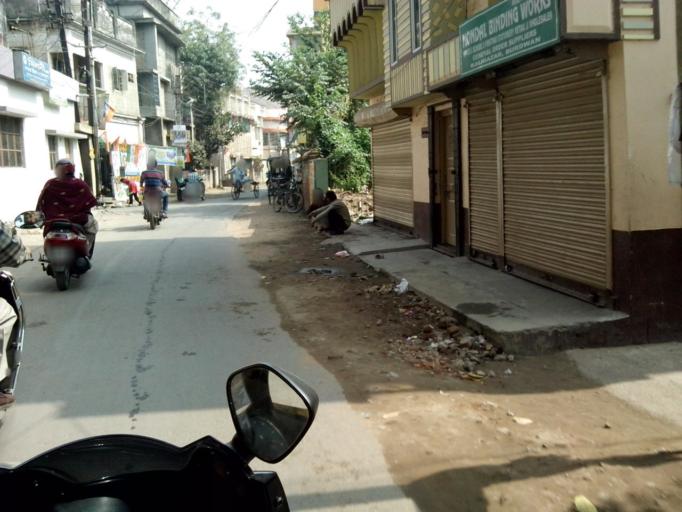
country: IN
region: West Bengal
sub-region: Barddhaman
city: Barddhaman
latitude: 23.2380
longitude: 87.8726
